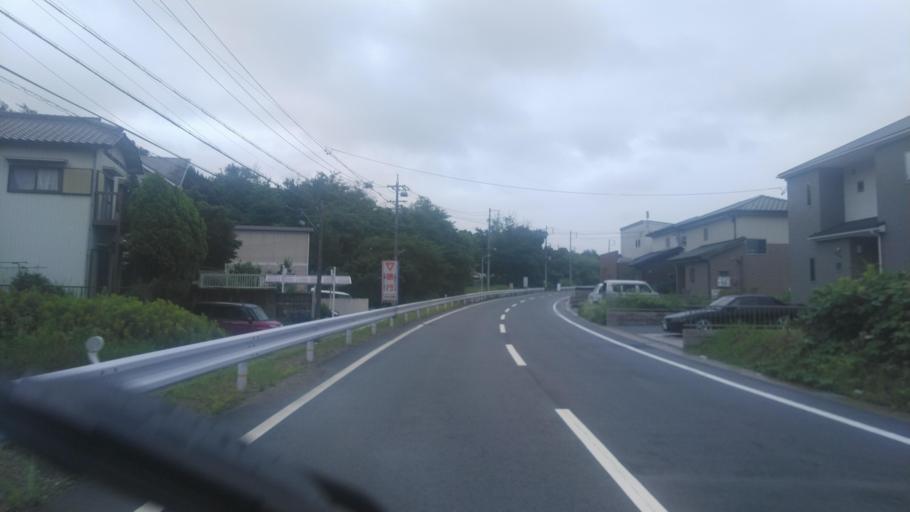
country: JP
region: Aichi
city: Kasugai
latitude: 35.2414
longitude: 137.0250
